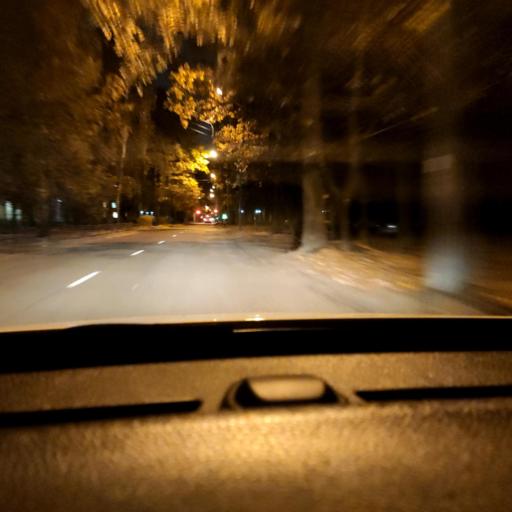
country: RU
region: Voronezj
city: Voronezh
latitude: 51.7214
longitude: 39.2184
